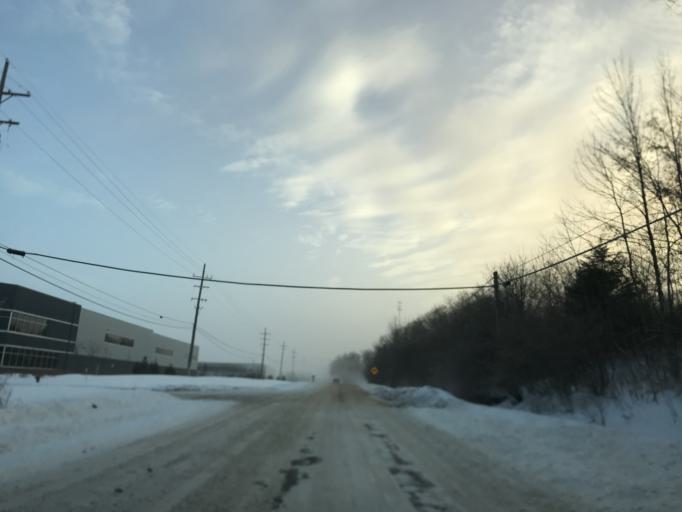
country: US
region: Michigan
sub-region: Oakland County
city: Wixom
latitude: 42.4927
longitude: -83.5636
